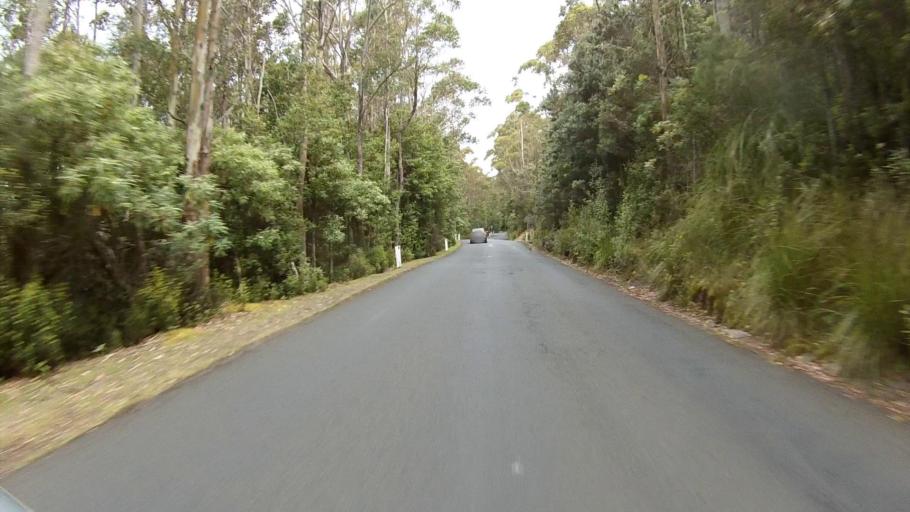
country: AU
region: Tasmania
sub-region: Hobart
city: Dynnyrne
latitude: -42.9123
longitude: 147.2448
